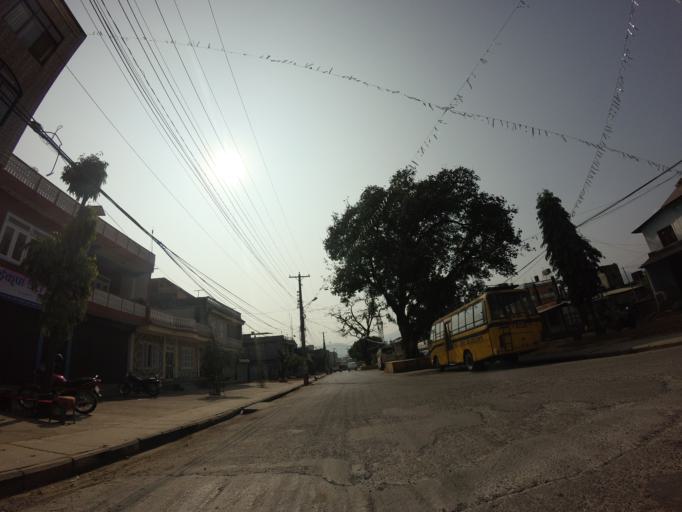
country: NP
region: Western Region
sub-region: Gandaki Zone
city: Pokhara
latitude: 28.2144
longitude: 83.9821
